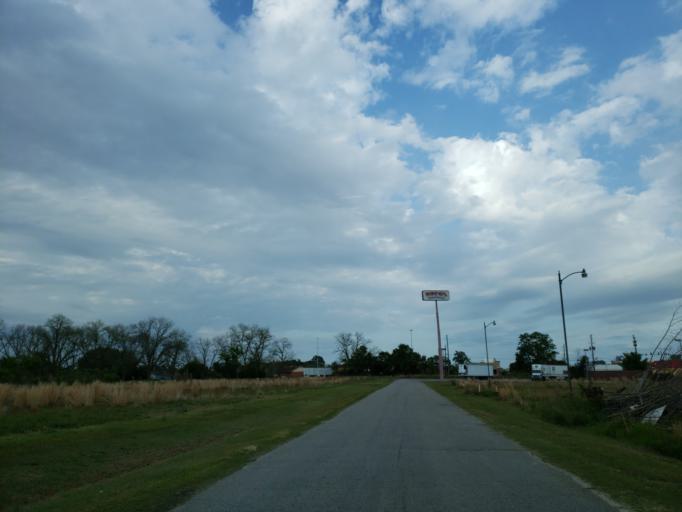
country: US
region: Georgia
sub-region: Dooly County
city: Vienna
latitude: 32.0876
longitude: -83.7676
